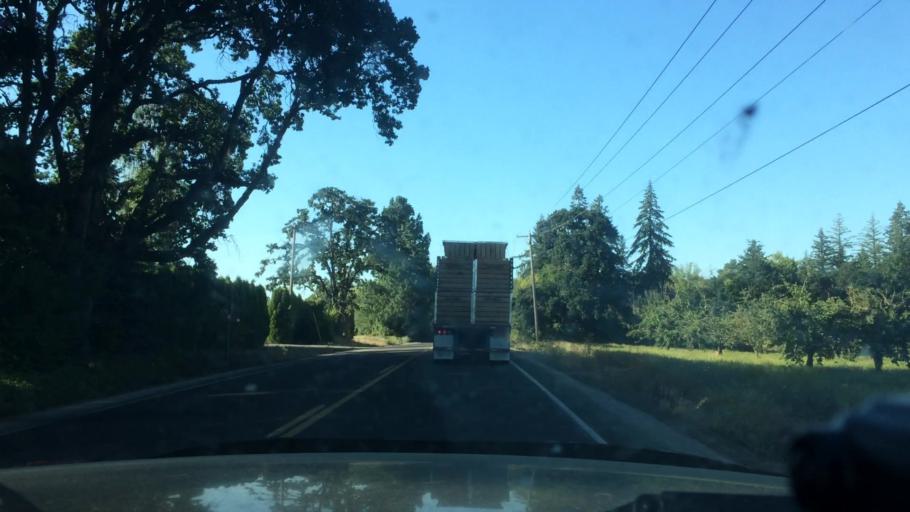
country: US
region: Oregon
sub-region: Marion County
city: Hayesville
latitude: 45.0700
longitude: -122.9796
